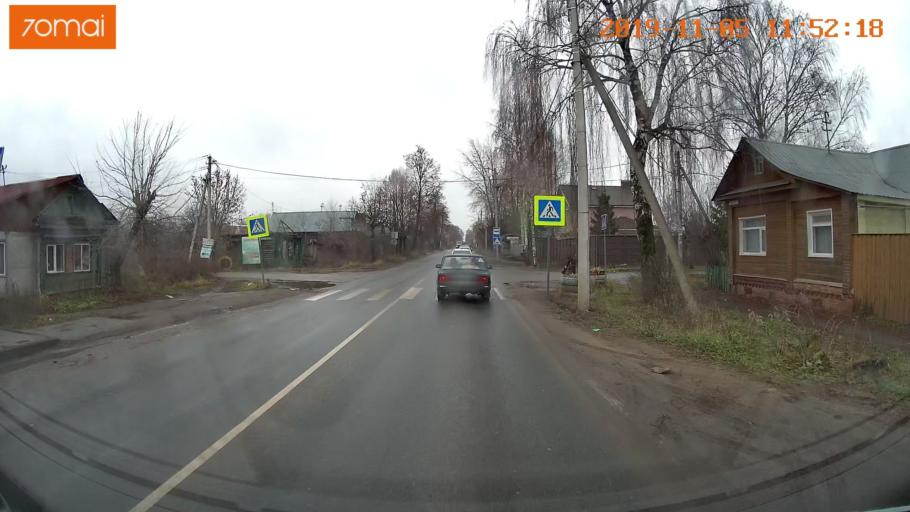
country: RU
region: Ivanovo
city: Bogorodskoye
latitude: 57.0006
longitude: 41.0293
